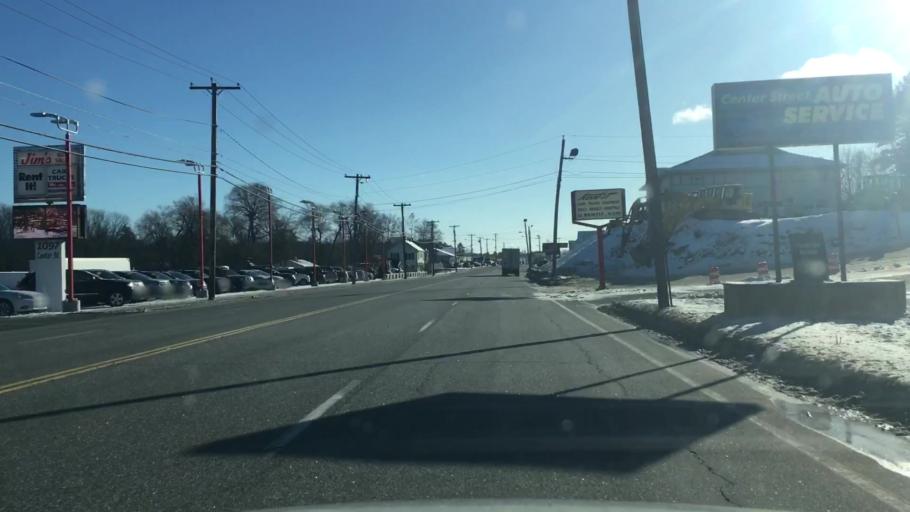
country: US
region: Maine
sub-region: Androscoggin County
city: Lewiston
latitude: 44.1391
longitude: -70.2261
